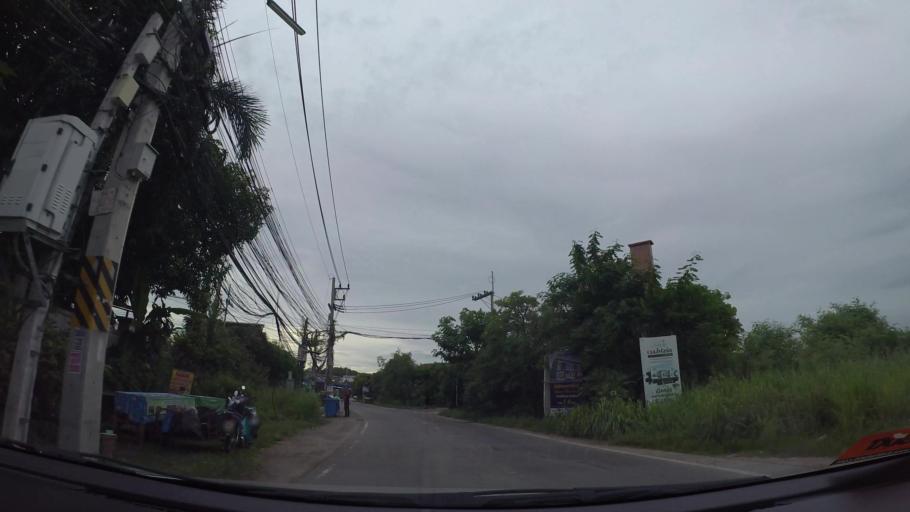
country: TH
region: Chon Buri
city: Si Racha
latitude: 13.1436
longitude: 100.9594
